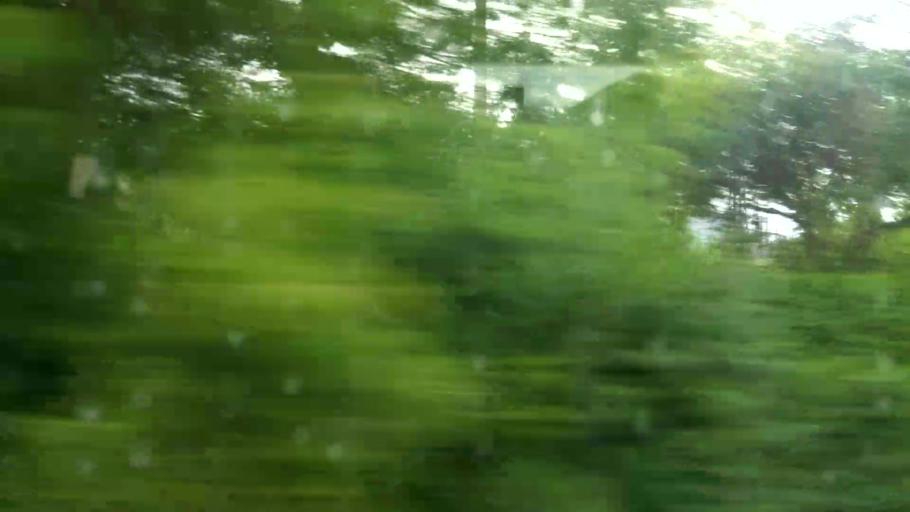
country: RU
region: Moskovskaya
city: Ozherel'ye
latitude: 54.8530
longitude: 38.2524
